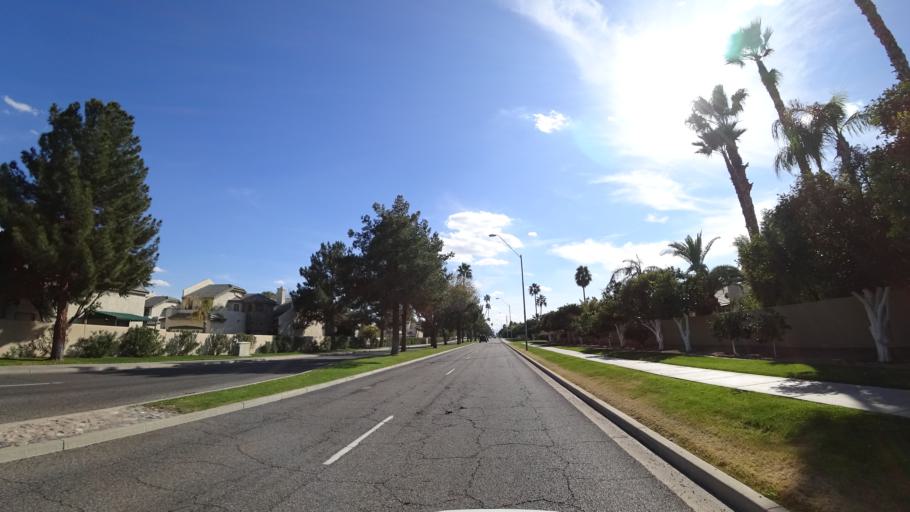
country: US
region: Arizona
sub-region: Maricopa County
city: Sun City
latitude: 33.6644
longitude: -112.2205
